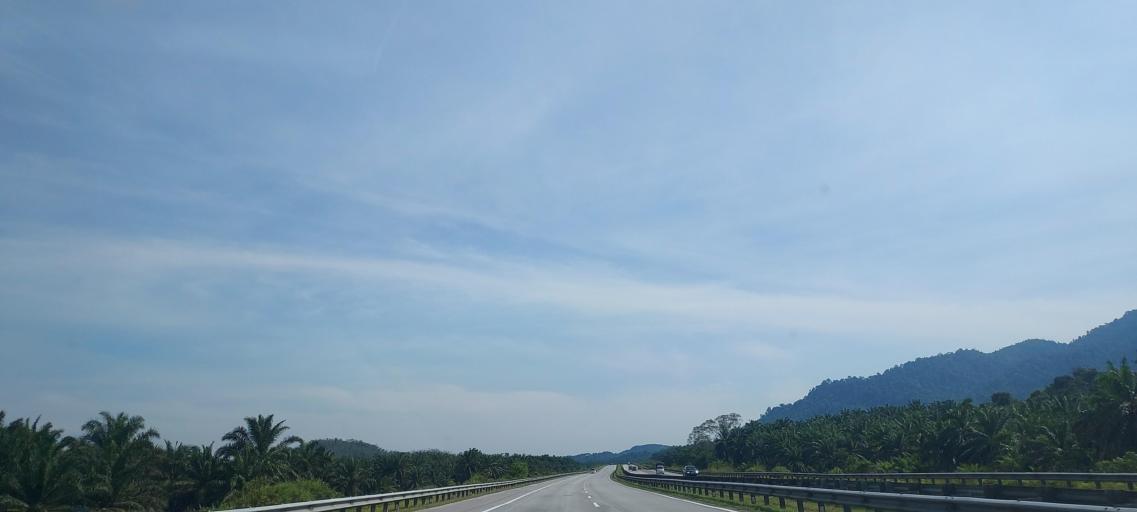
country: MY
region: Terengganu
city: Marang
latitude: 4.9667
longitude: 103.0810
